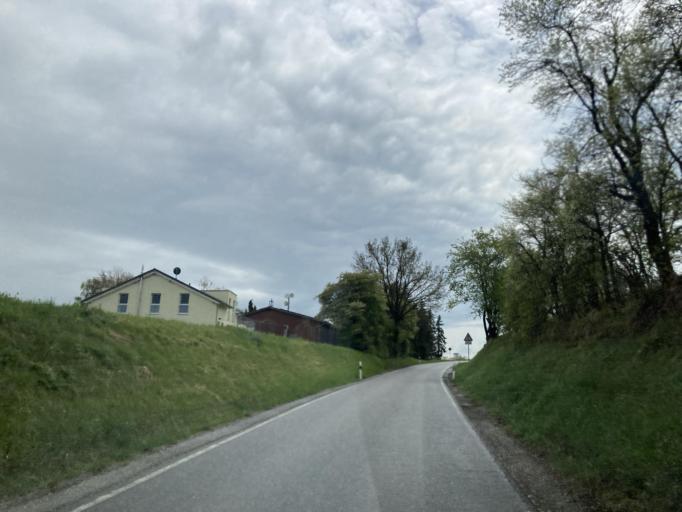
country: DE
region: Baden-Wuerttemberg
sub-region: Regierungsbezirk Stuttgart
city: Herrenberg
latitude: 48.5472
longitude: 8.8796
